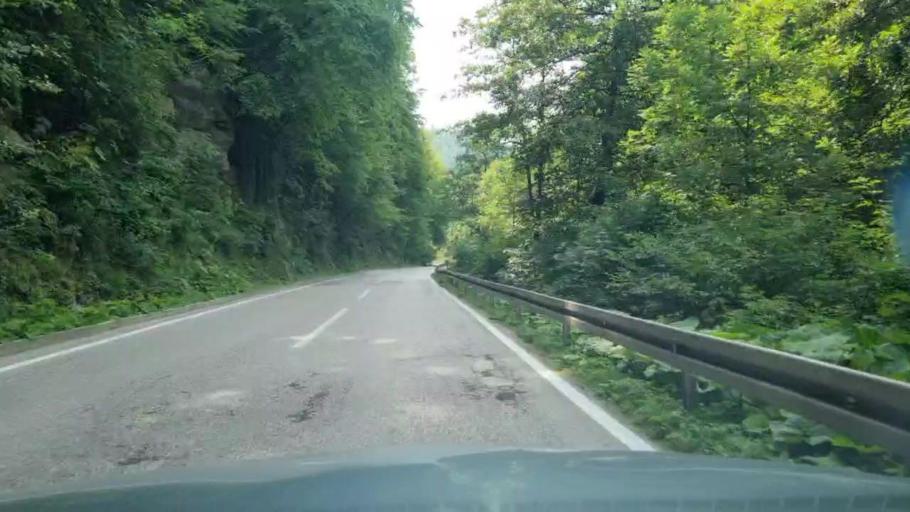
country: BA
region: Federation of Bosnia and Herzegovina
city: Kladanj
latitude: 44.2343
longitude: 18.7232
